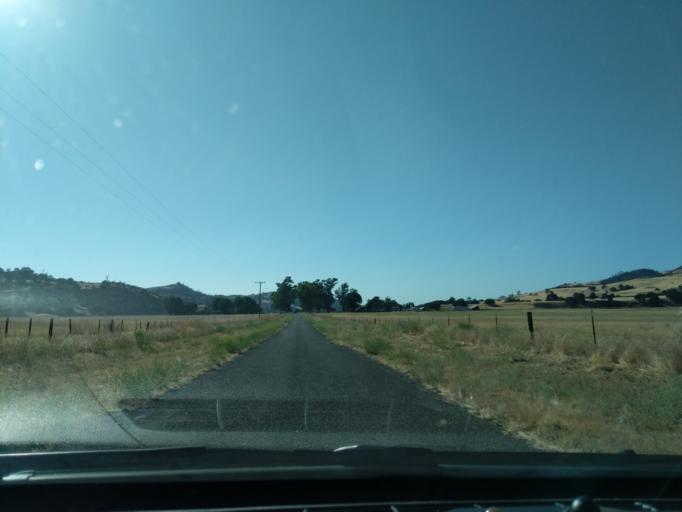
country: US
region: California
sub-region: Fresno County
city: Coalinga
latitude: 36.1087
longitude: -120.7146
